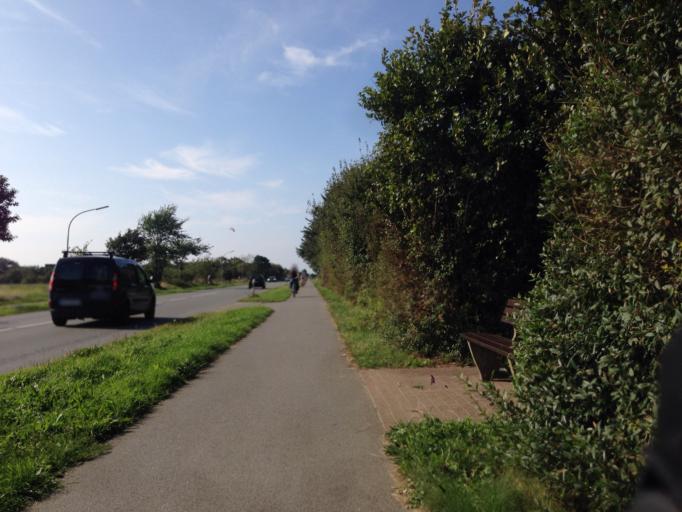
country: DE
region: Schleswig-Holstein
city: Tinnum
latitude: 54.8987
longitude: 8.3511
